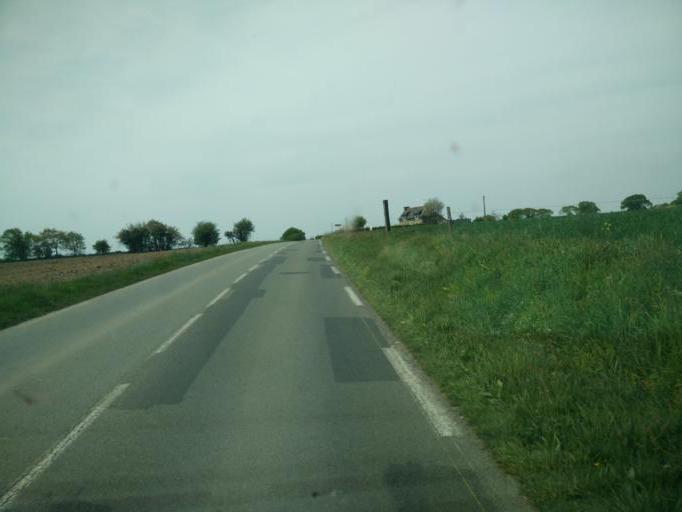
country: FR
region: Brittany
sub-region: Departement des Cotes-d'Armor
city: Matignon
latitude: 48.6062
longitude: -2.3038
